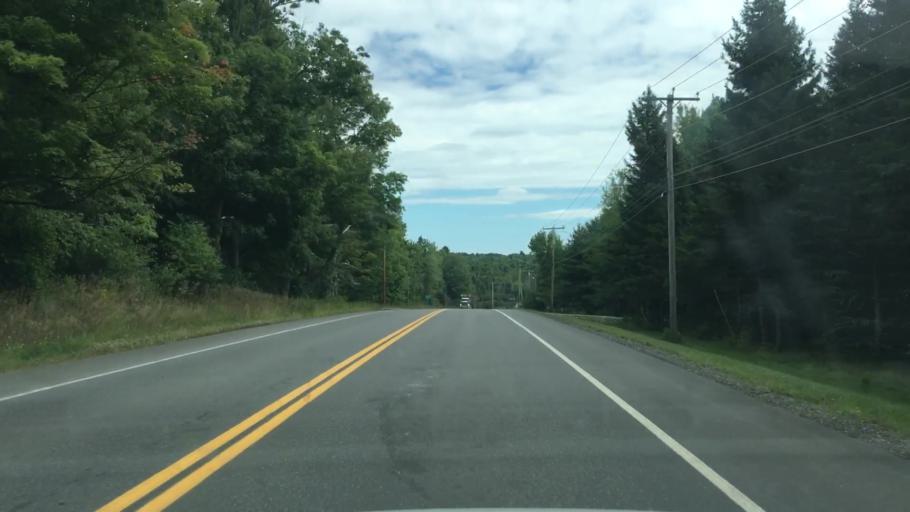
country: US
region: Maine
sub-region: Piscataquis County
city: Milo
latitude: 45.2412
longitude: -69.0396
